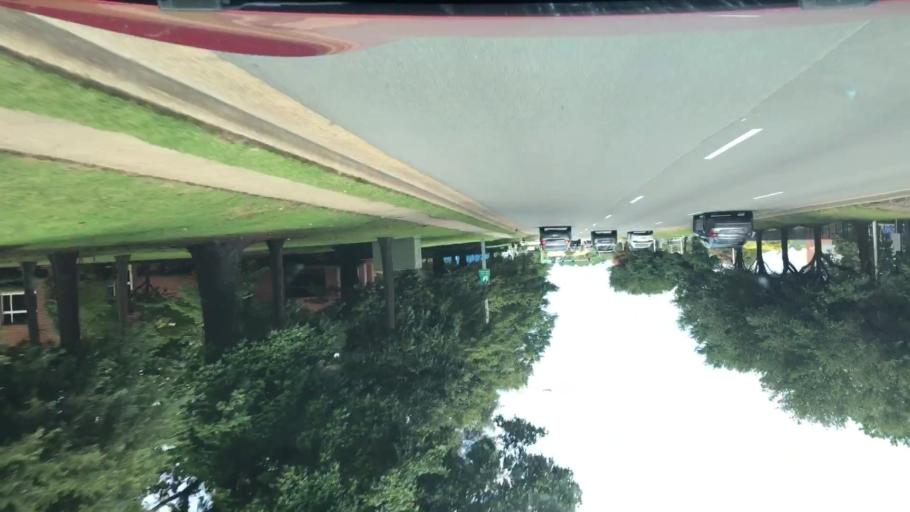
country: US
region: Virginia
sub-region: City of Chesapeake
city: Chesapeake
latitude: 36.8692
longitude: -76.1331
